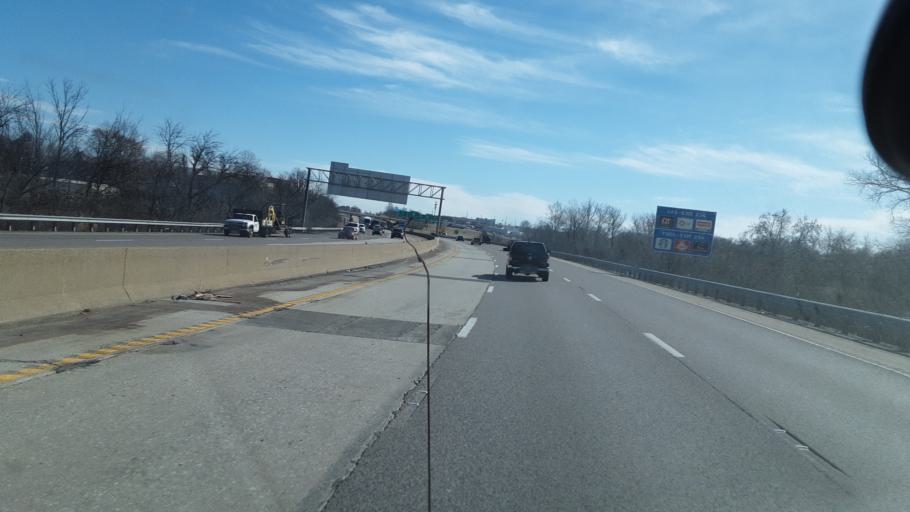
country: US
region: Missouri
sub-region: Saint Louis County
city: Bridgeton
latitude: 38.7441
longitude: -90.4194
